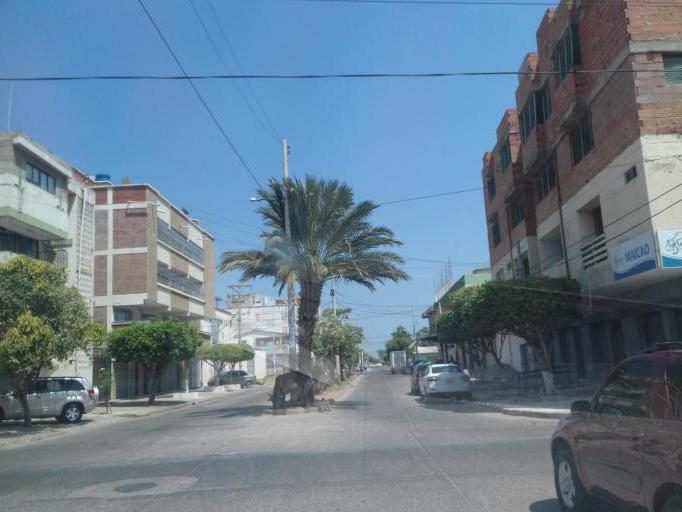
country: CO
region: La Guajira
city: Maicao
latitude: 11.3769
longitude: -72.2362
